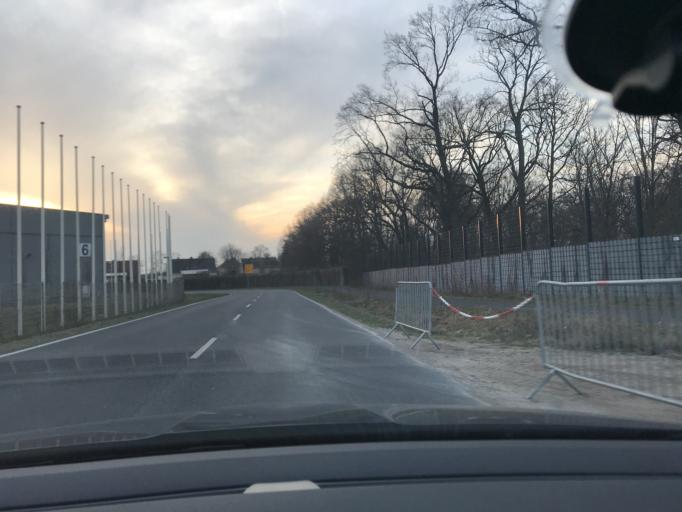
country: DE
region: Brandenburg
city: Schonefeld
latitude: 52.3532
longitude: 13.4751
